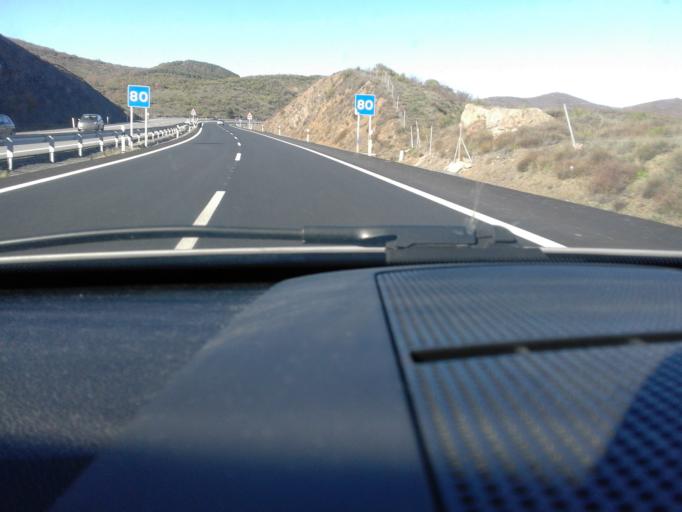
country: ES
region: Castille and Leon
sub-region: Provincia de Leon
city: Soto y Amio
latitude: 42.8098
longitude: -5.8367
